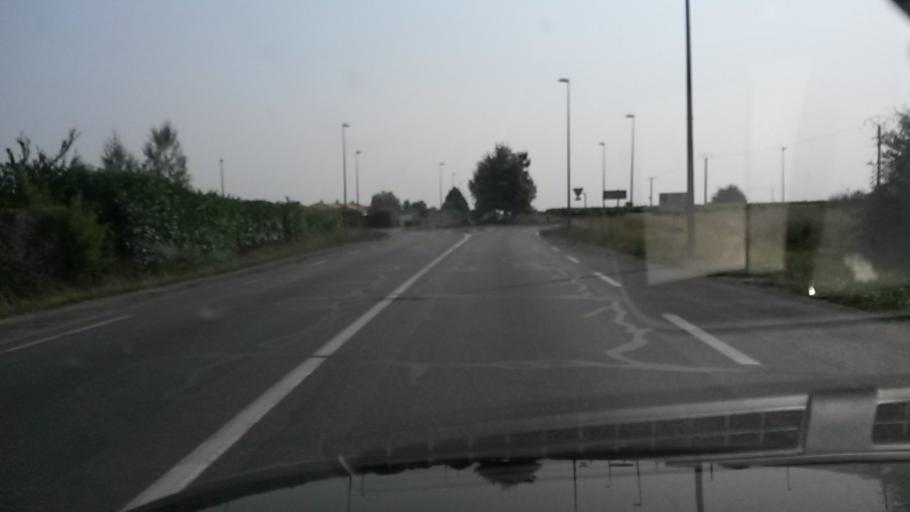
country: FR
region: Pays de la Loire
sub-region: Departement de la Loire-Atlantique
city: Mouzillon
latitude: 47.1456
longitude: -1.2814
